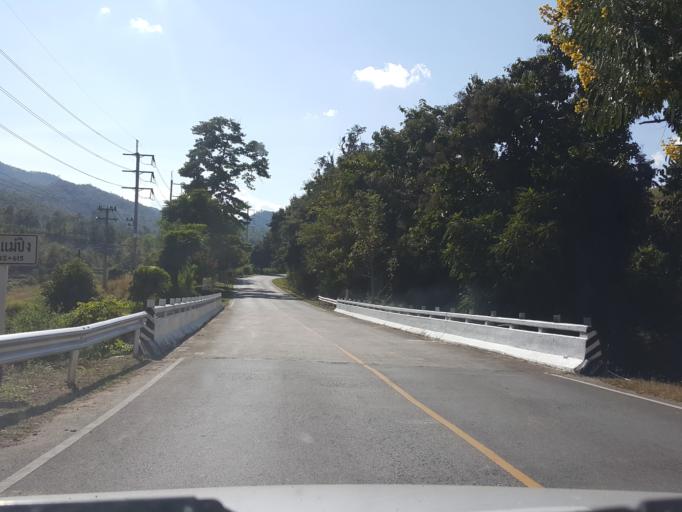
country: TH
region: Mae Hong Son
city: Mae Hi
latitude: 19.2864
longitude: 98.4812
